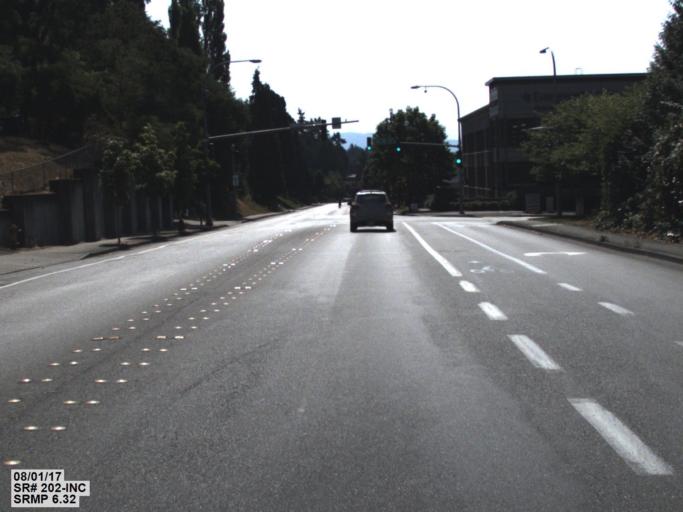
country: US
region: Washington
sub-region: King County
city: Redmond
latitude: 47.6830
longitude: -122.1238
